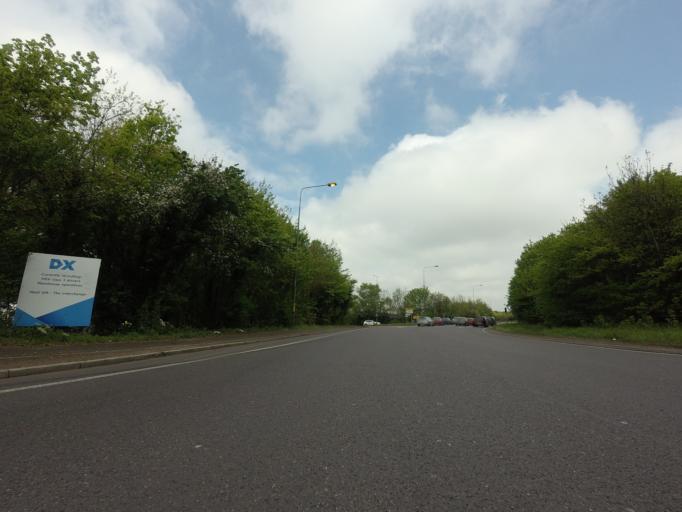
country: GB
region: England
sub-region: Kent
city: Swanley
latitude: 51.3872
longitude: 0.1921
